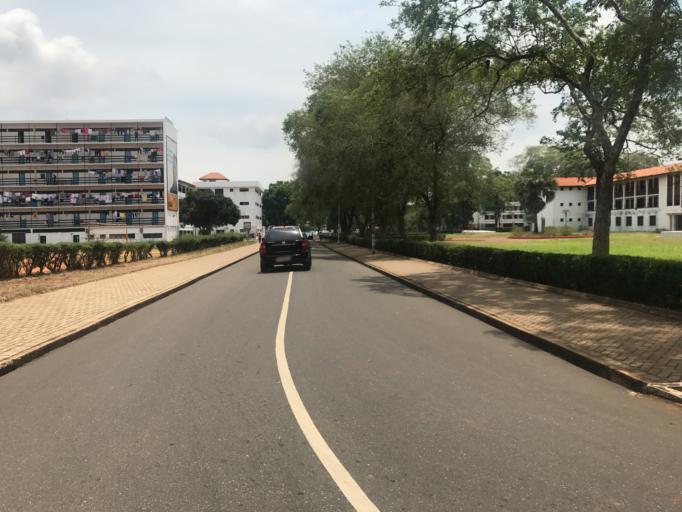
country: GH
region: Greater Accra
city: Medina Estates
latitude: 5.6466
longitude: -0.1860
